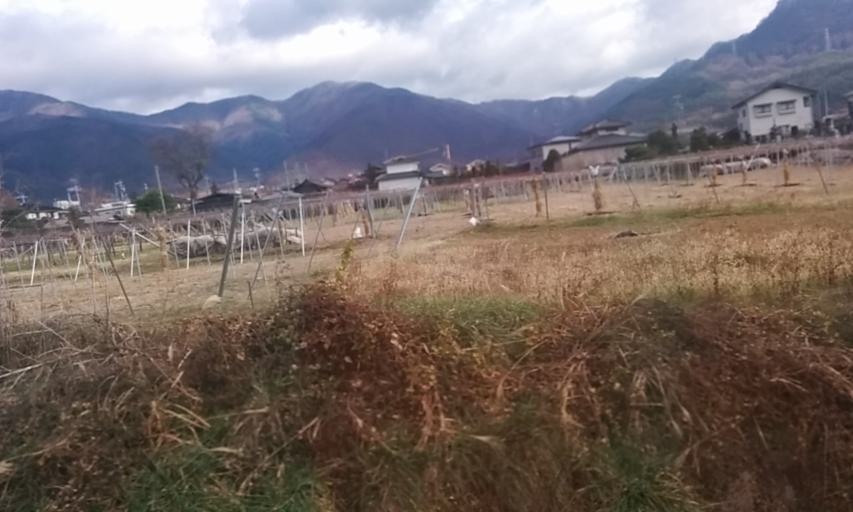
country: JP
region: Nagano
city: Ueda
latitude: 36.4396
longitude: 138.1885
